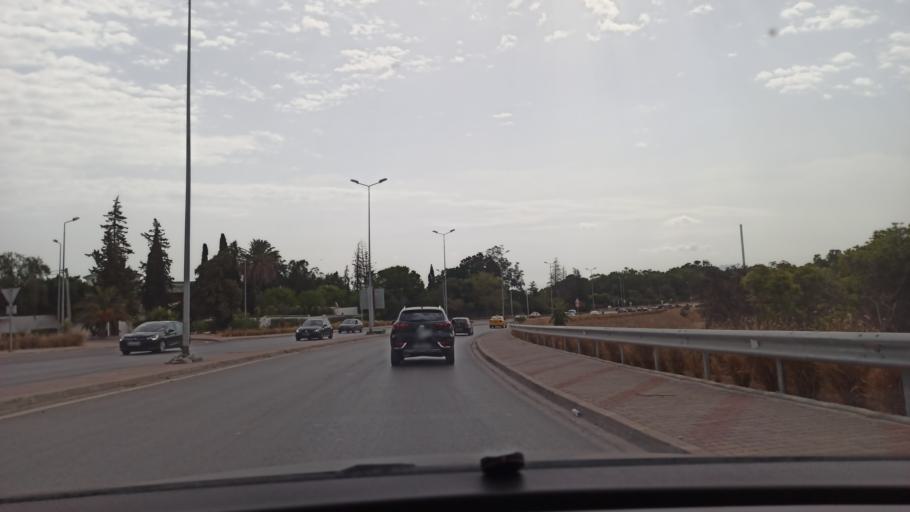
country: TN
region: Tunis
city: Tunis
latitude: 36.8299
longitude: 10.1641
